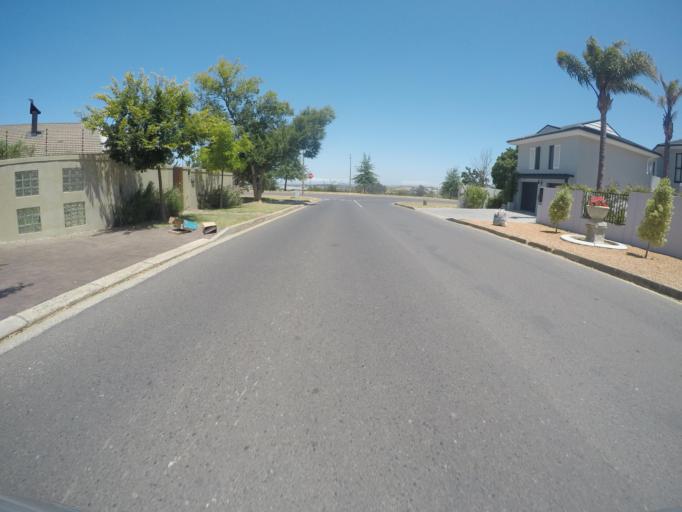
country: ZA
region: Western Cape
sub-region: Cape Winelands District Municipality
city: Stellenbosch
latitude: -33.9653
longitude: 18.8533
